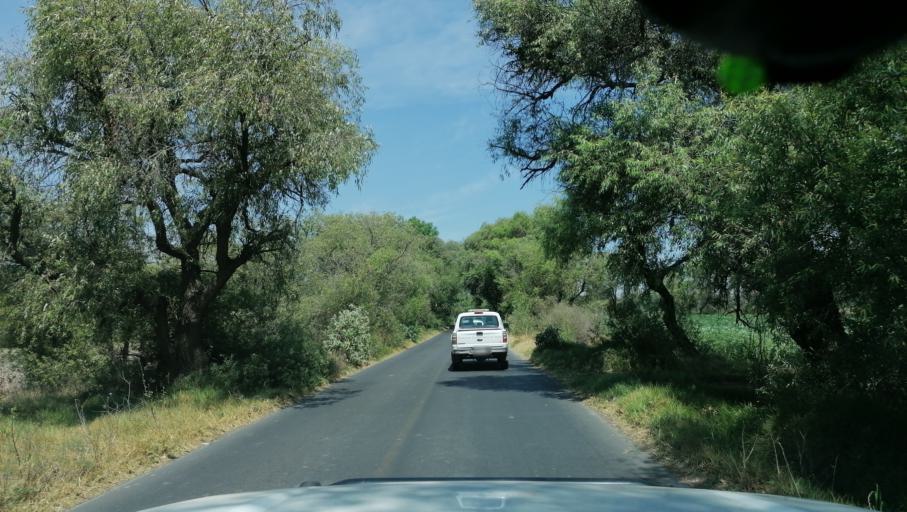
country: MX
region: Tlaxcala
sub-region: Tetlatlahuca
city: Tetlatlahuca
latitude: 19.2041
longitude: -98.2835
